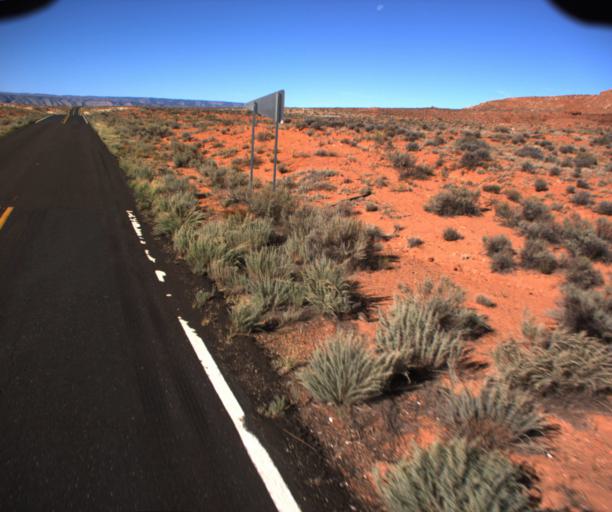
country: US
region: Arizona
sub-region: Coconino County
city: Page
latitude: 36.6849
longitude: -111.8402
